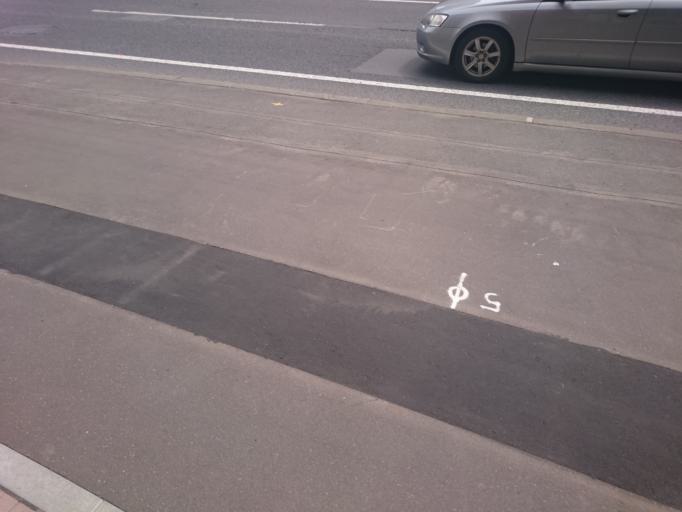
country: JP
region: Hokkaido
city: Sapporo
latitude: 43.0633
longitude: 141.3623
